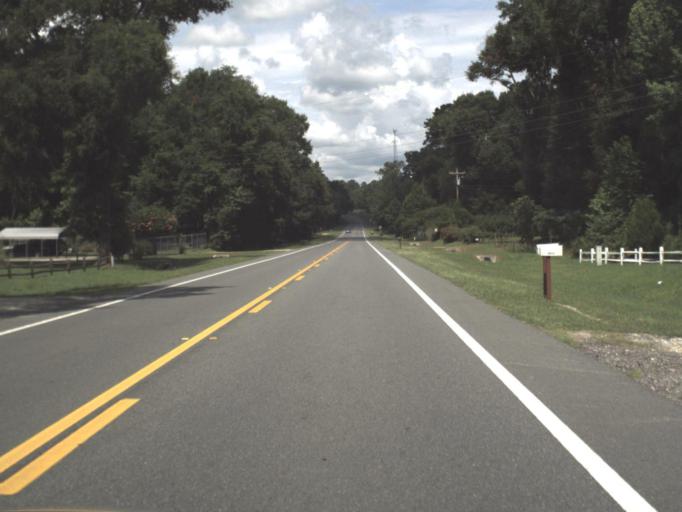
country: US
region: Florida
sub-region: Alachua County
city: Alachua
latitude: 29.8038
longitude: -82.4839
